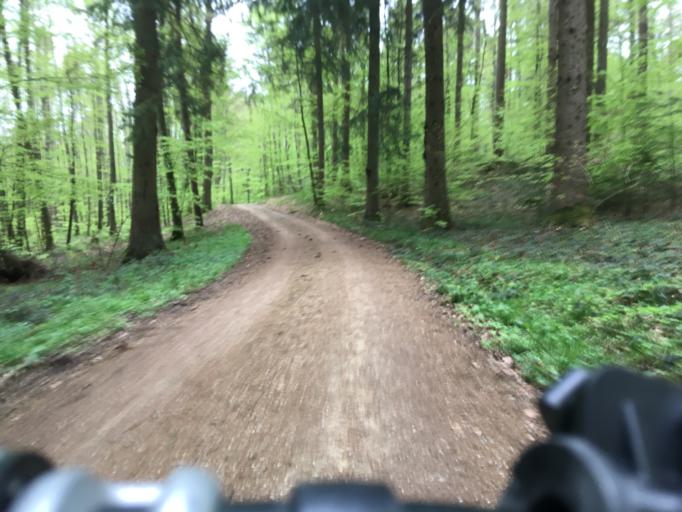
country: DE
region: Baden-Wuerttemberg
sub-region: Freiburg Region
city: Gailingen
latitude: 47.7093
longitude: 8.7318
